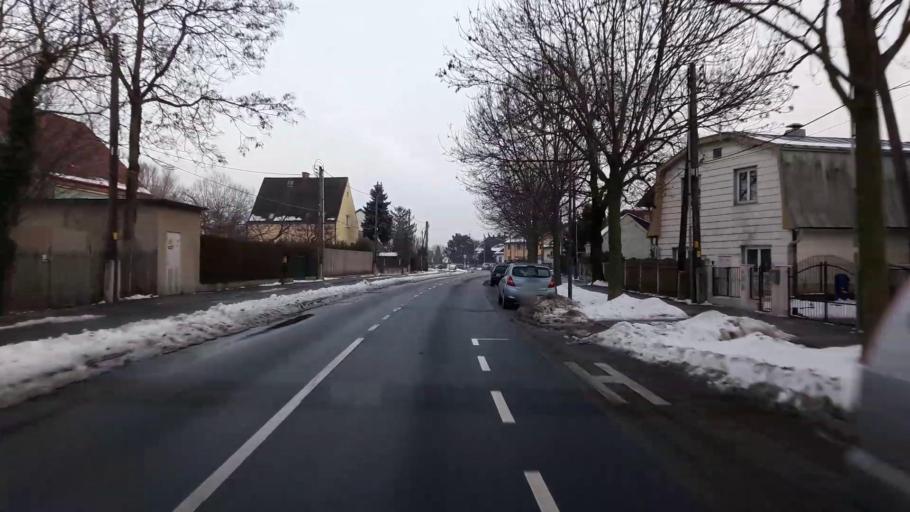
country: AT
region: Vienna
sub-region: Wien Stadt
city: Vienna
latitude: 48.2471
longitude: 16.4032
